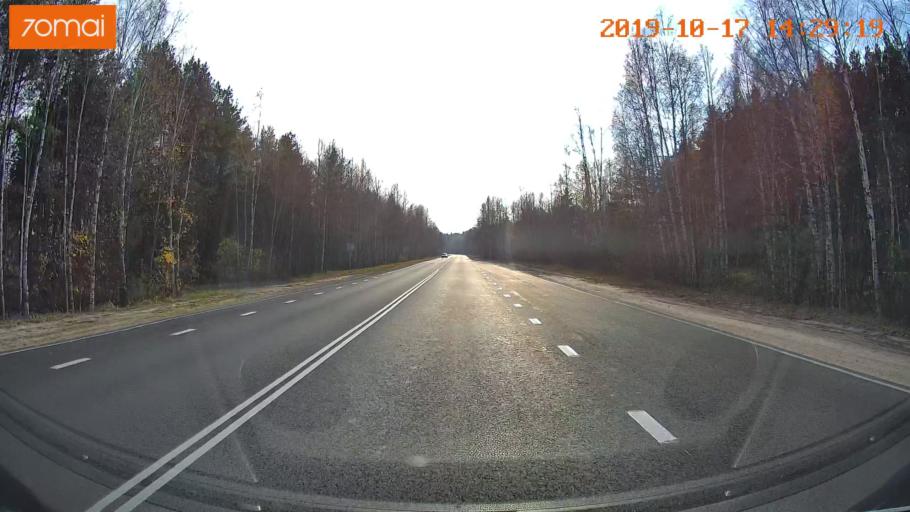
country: RU
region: Rjazan
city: Solotcha
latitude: 54.9622
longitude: 39.9430
